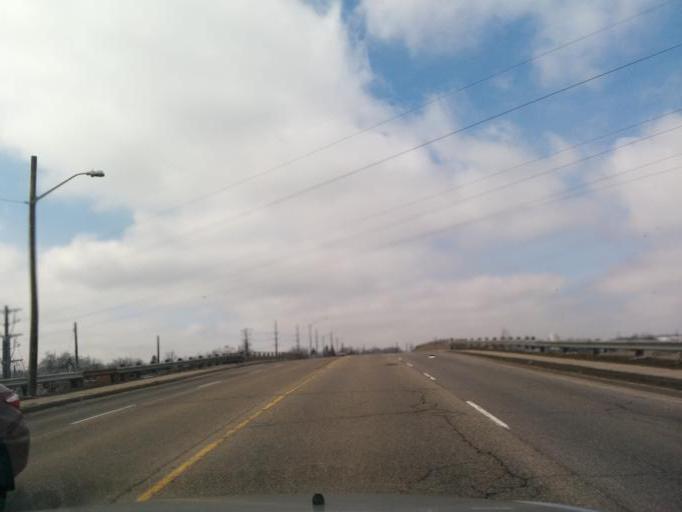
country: CA
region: Ontario
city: Waterloo
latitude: 43.4924
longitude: -80.5405
